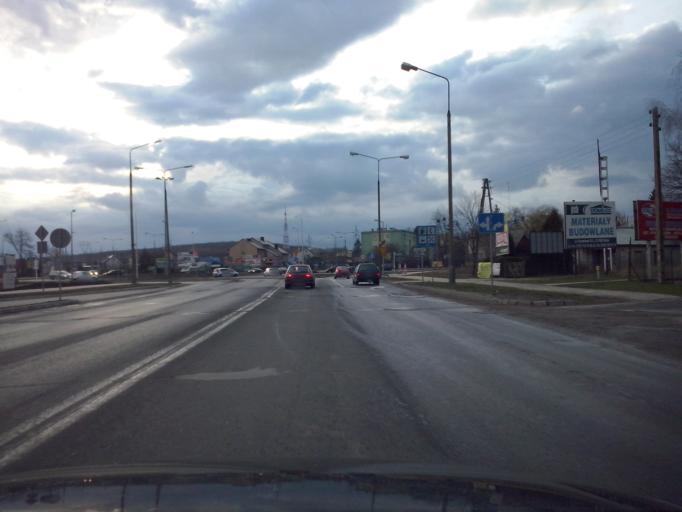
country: PL
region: Lublin Voivodeship
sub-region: Chelm
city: Chelm
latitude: 51.1464
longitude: 23.4387
